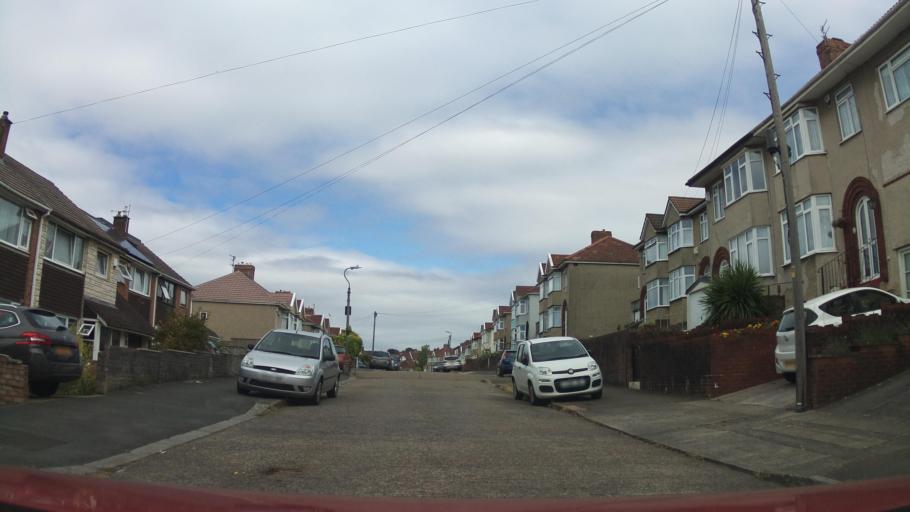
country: GB
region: England
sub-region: Bristol
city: Bristol
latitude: 51.4349
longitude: -2.5851
